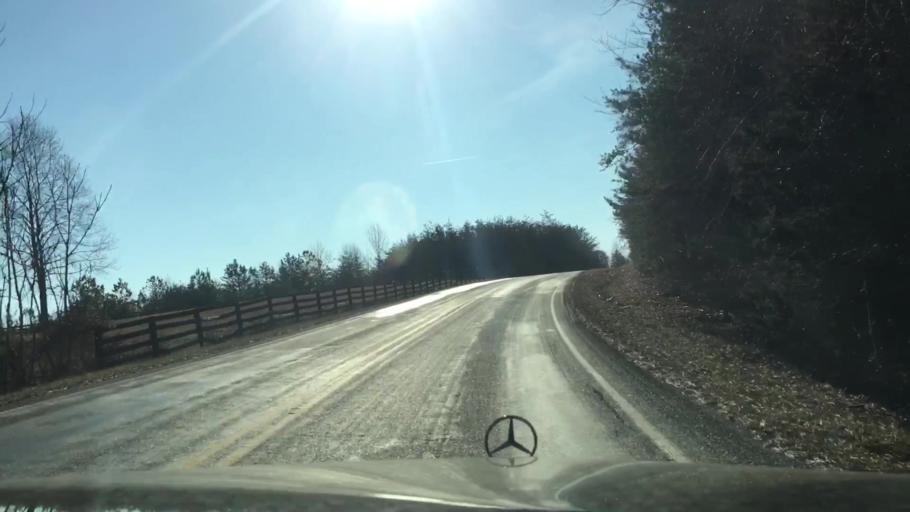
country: US
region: Virginia
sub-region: Pittsylvania County
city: Motley
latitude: 37.1811
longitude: -79.4109
